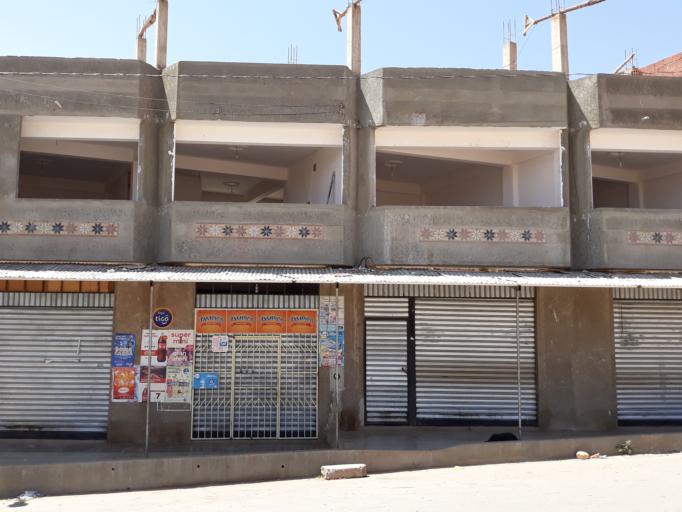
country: BO
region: Cochabamba
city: Cochabamba
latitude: -17.4630
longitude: -66.1354
